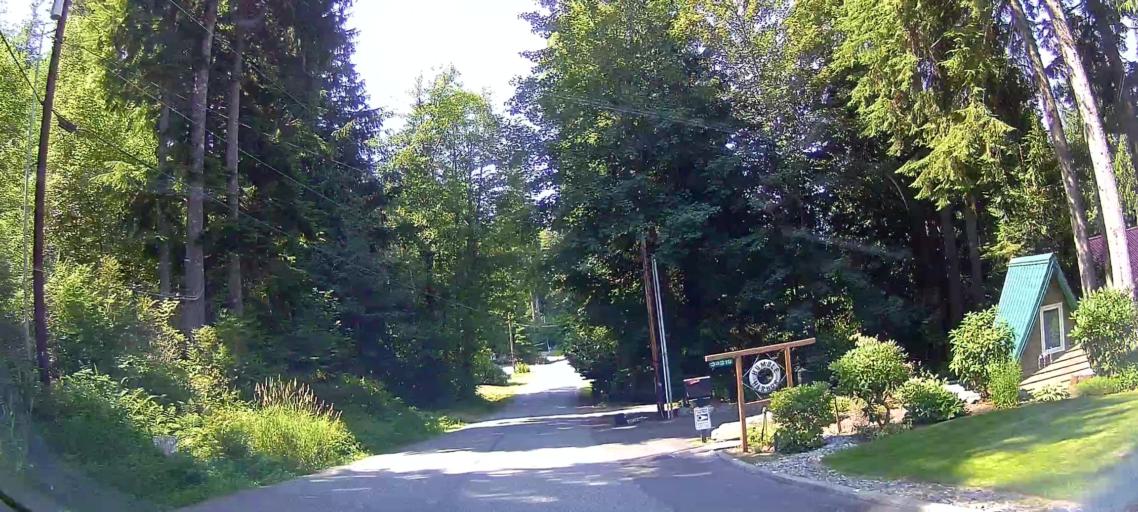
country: US
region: Washington
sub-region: Snohomish County
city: Arlington Heights
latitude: 48.3144
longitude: -122.0031
